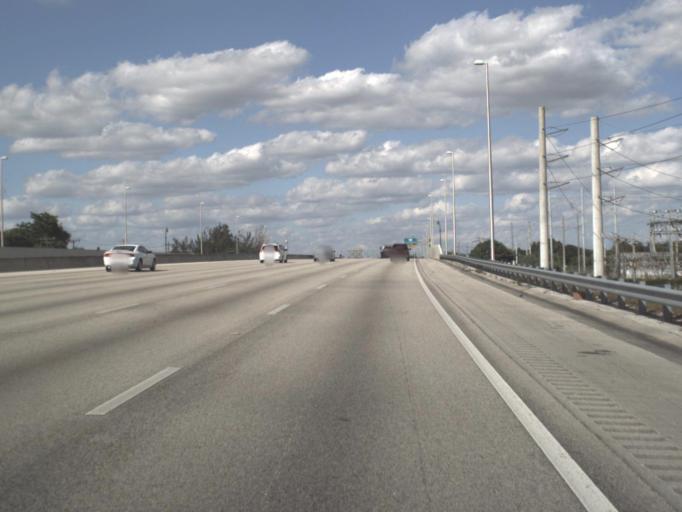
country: US
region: Florida
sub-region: Broward County
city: Plantation
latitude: 26.1188
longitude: -80.2182
